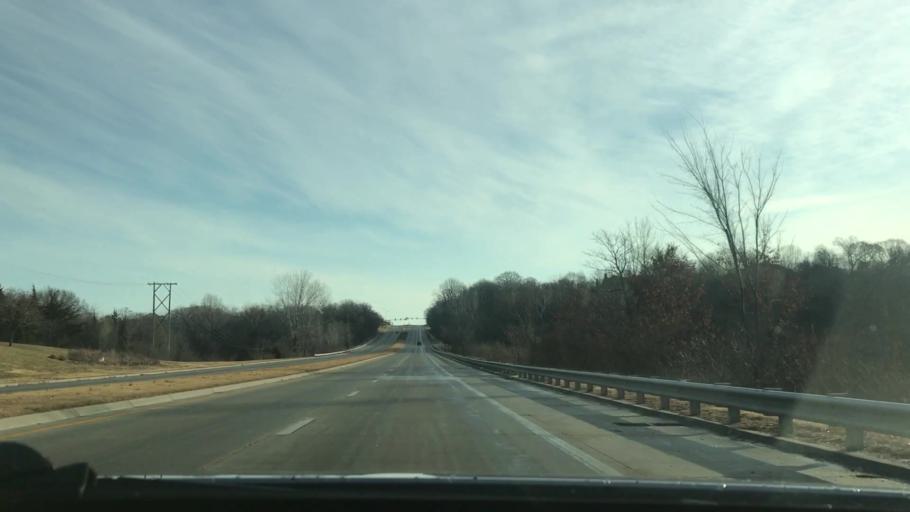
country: US
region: Missouri
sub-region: Platte County
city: Parkville
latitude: 39.2106
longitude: -94.6713
